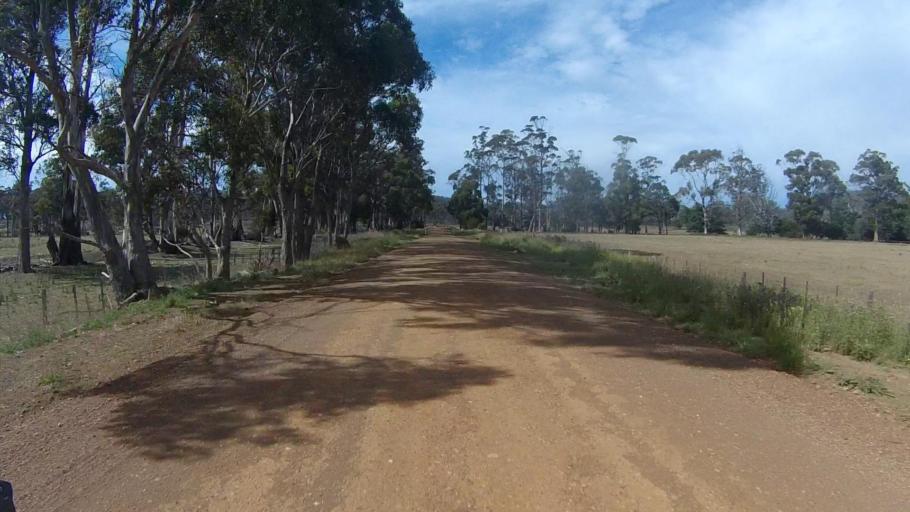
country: AU
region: Tasmania
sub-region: Sorell
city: Sorell
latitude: -42.6406
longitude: 147.9004
